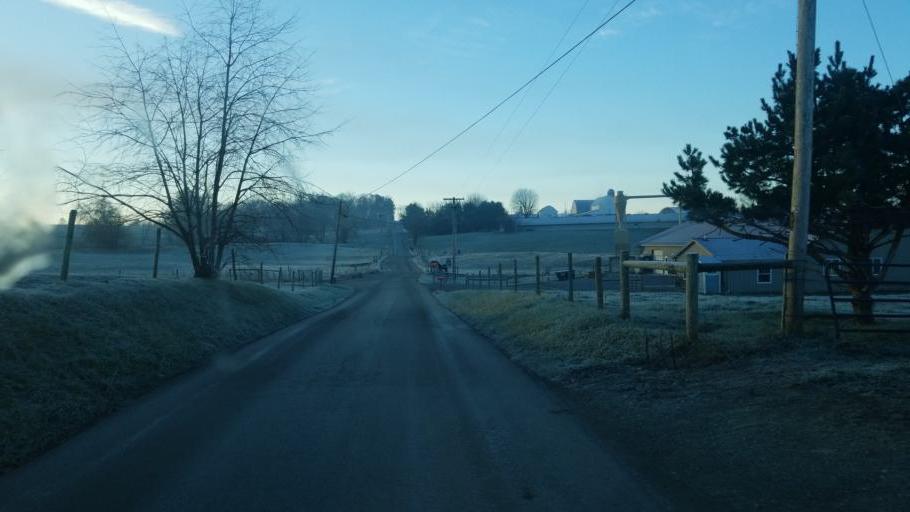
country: US
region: Ohio
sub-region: Holmes County
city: Millersburg
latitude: 40.5884
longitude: -81.8010
